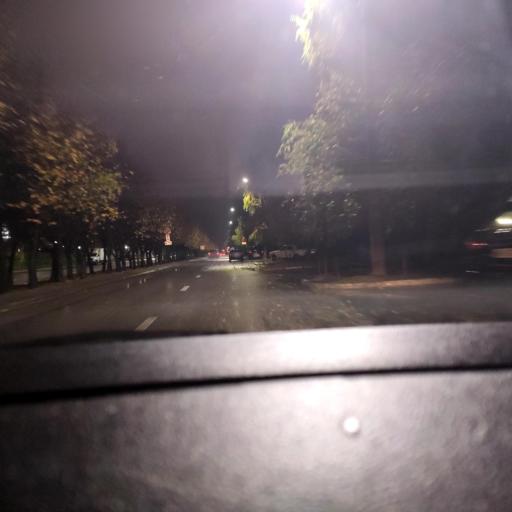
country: RU
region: Voronezj
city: Podgornoye
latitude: 51.7078
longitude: 39.1630
